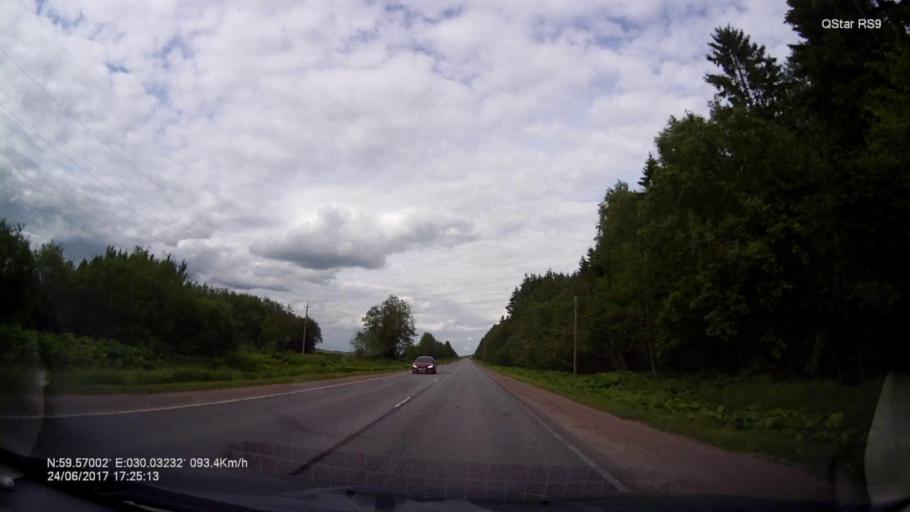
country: RU
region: Leningrad
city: Mariyenburg
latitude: 59.5702
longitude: 30.0328
